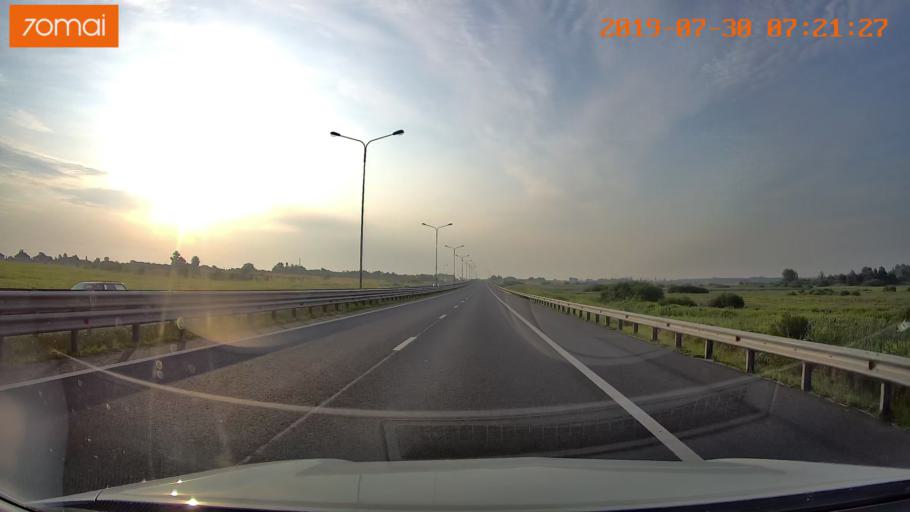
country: RU
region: Kaliningrad
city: Bol'shoe Isakovo
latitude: 54.6964
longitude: 20.7290
